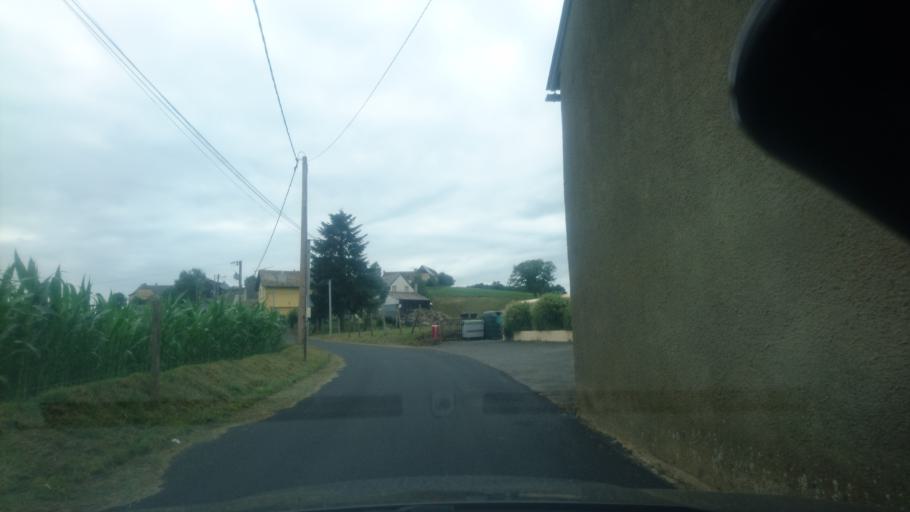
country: FR
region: Midi-Pyrenees
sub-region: Departement des Hautes-Pyrenees
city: Horgues
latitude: 43.1217
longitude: 0.0651
